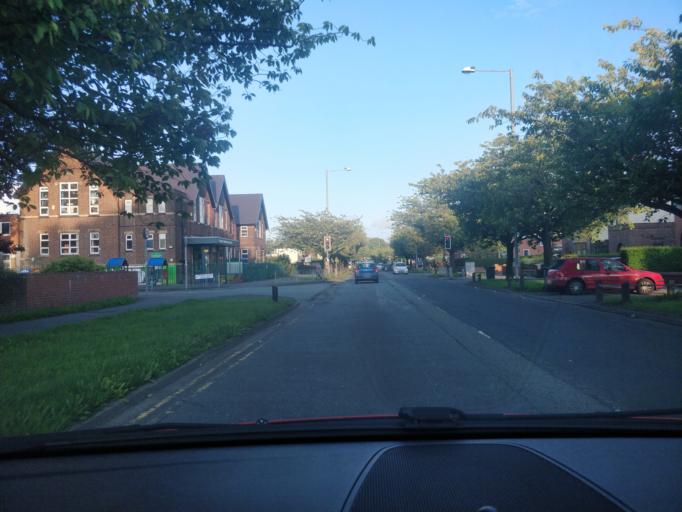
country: GB
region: England
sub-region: Lancashire
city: Preston
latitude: 53.7738
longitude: -2.6862
